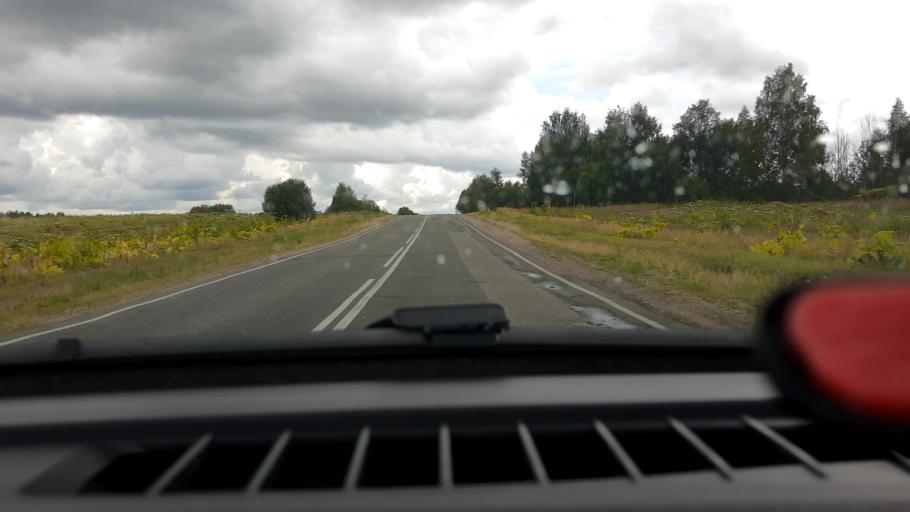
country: RU
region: Nizjnij Novgorod
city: Sitniki
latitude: 56.4972
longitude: 44.0012
